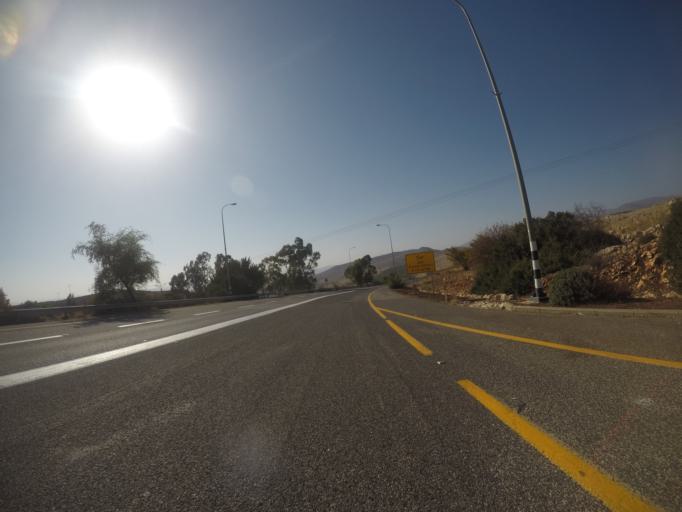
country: IL
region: Northern District
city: Rosh Pinna
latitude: 32.9045
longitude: 35.5473
